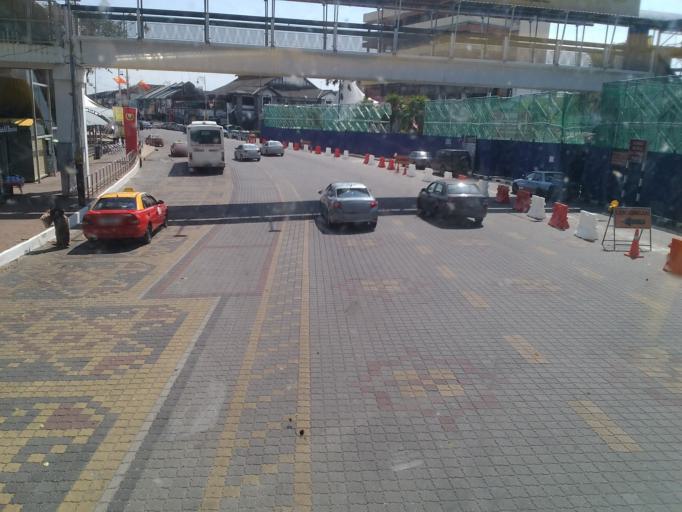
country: MY
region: Kedah
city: Alor Setar
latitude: 6.1175
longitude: 100.3668
